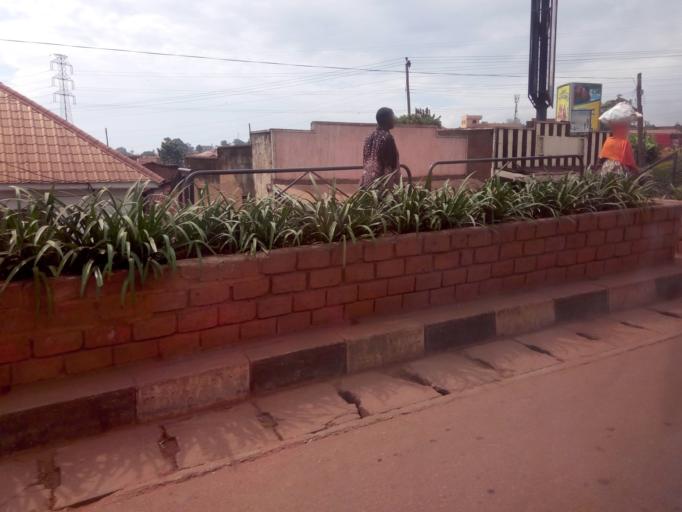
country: UG
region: Central Region
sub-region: Kampala District
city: Kampala
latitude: 0.2942
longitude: 32.5729
